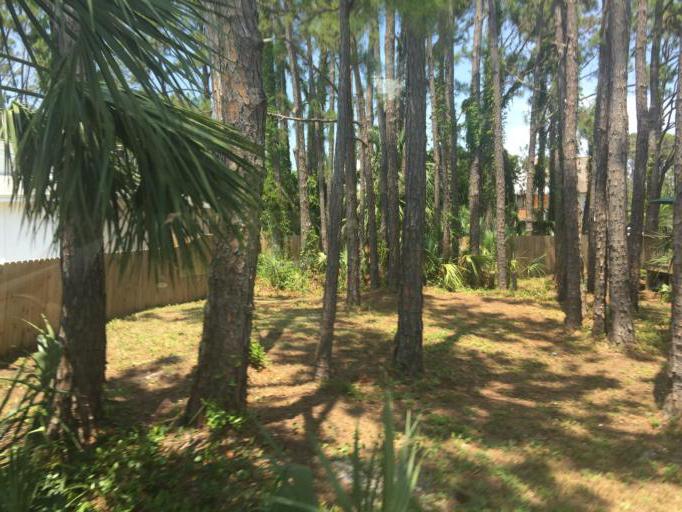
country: US
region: Florida
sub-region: Bay County
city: Lower Grand Lagoon
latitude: 30.1510
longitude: -85.7608
